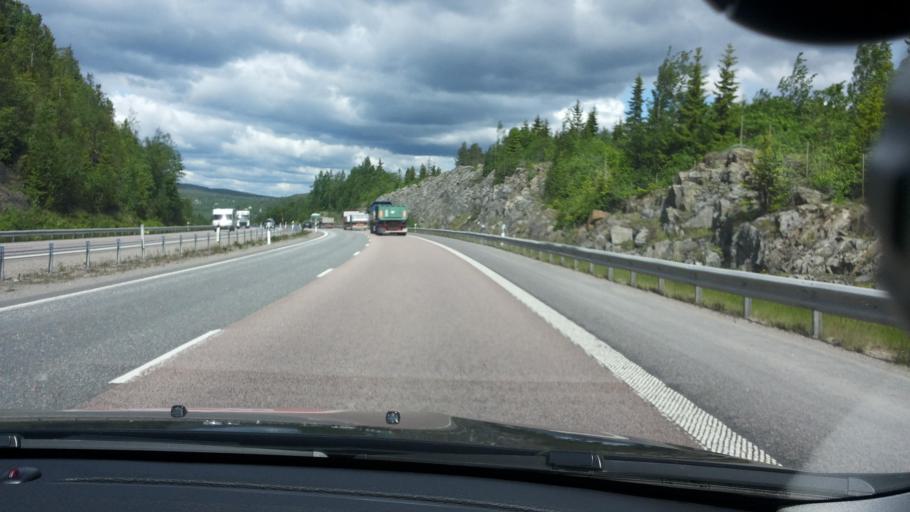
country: SE
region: Vaesternorrland
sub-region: Sundsvalls Kommun
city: Sundsbruk
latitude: 62.4630
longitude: 17.3379
